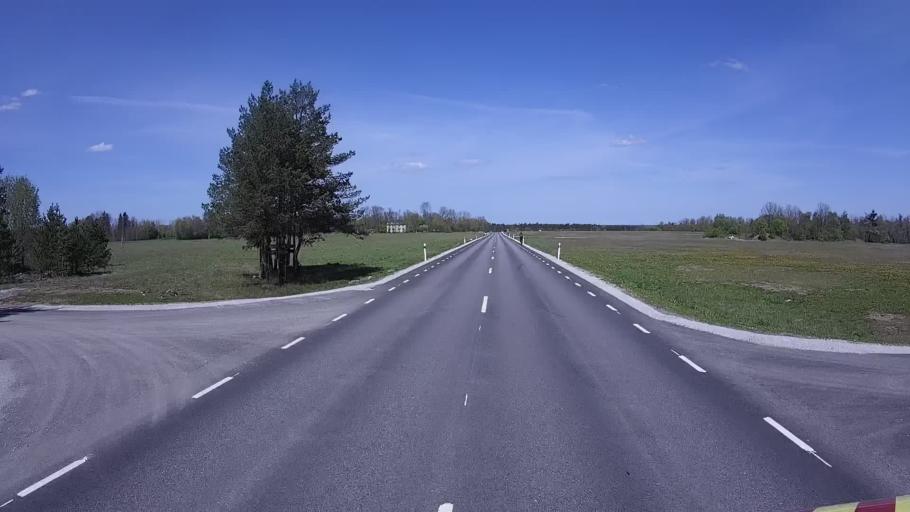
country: EE
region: Harju
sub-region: Paldiski linn
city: Paldiski
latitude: 59.2060
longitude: 24.0958
